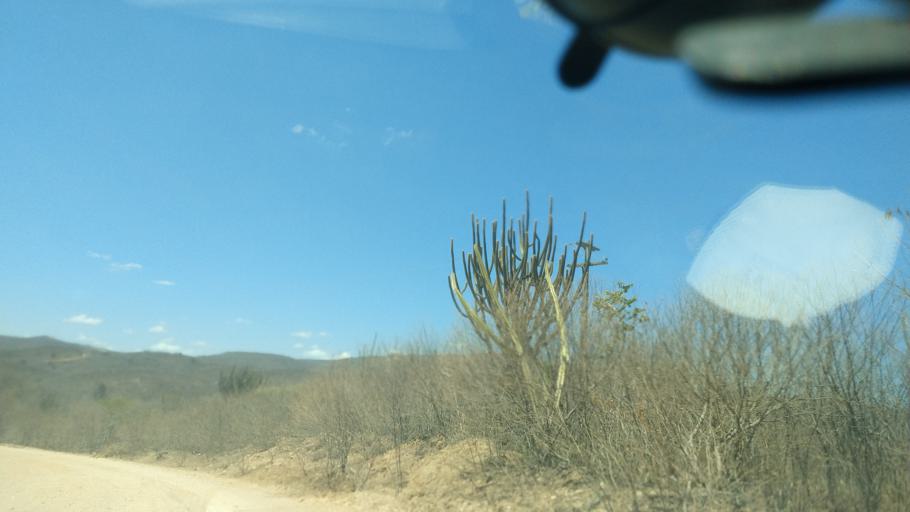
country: BR
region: Rio Grande do Norte
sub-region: Cerro Cora
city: Cerro Cora
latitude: -6.0097
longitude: -36.2912
